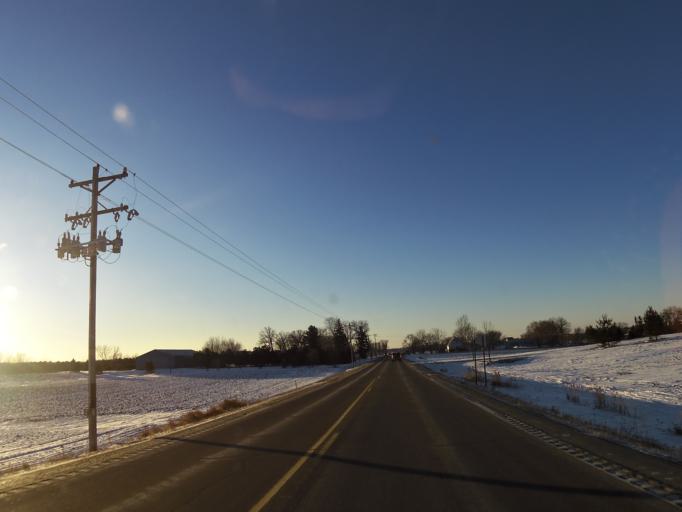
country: US
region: Minnesota
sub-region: Scott County
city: Prior Lake
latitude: 44.6767
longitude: -93.3792
